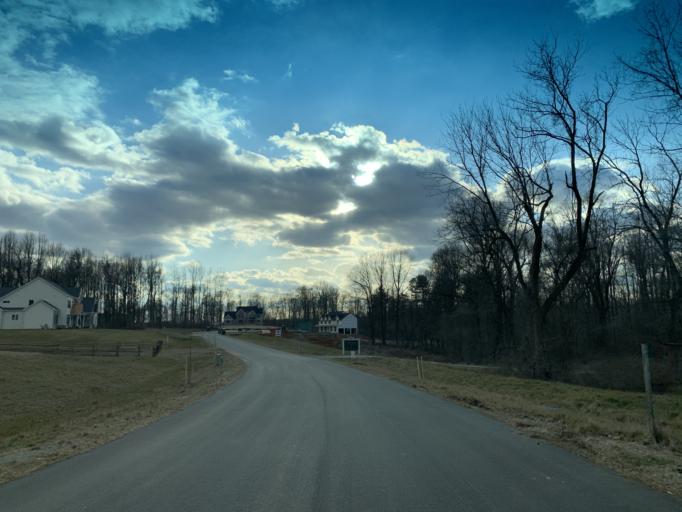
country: US
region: Maryland
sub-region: Harford County
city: Bel Air South
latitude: 39.4932
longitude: -76.2810
